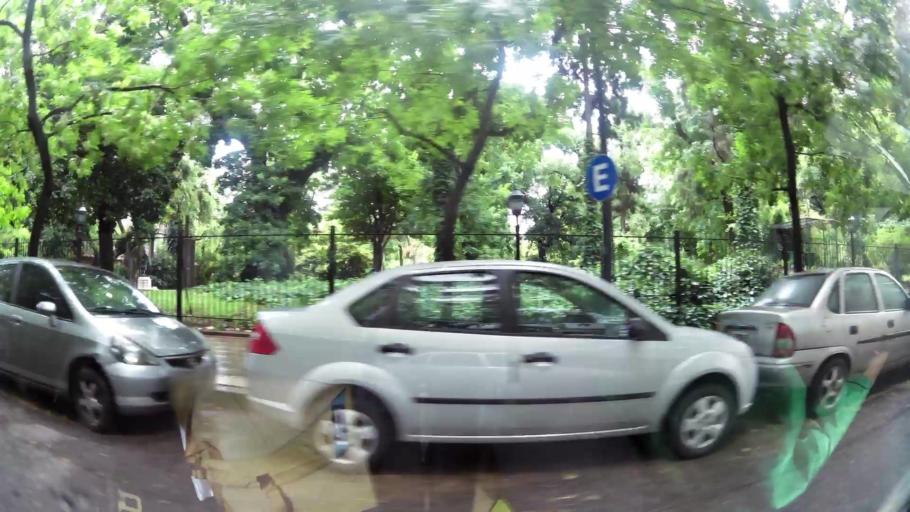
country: AR
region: Buenos Aires F.D.
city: Retiro
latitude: -34.5830
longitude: -58.4153
